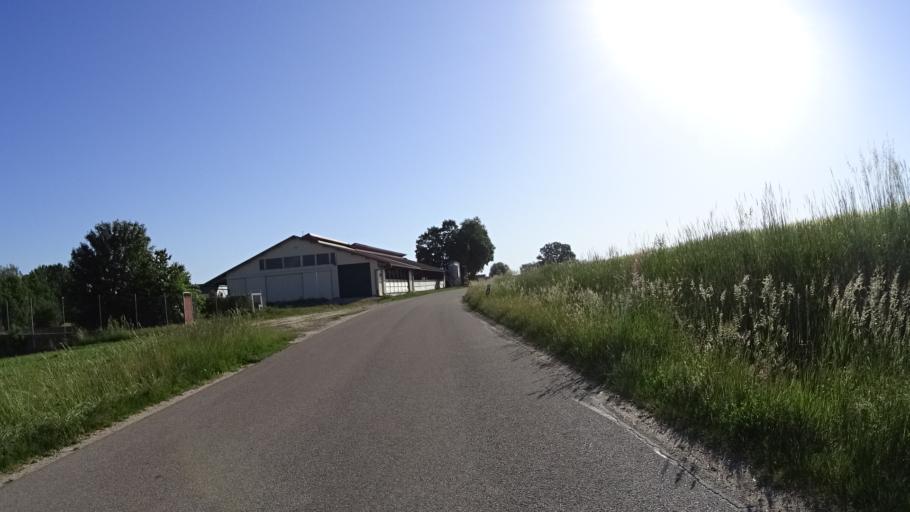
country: DE
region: Bavaria
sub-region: Regierungsbezirk Mittelfranken
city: Burk
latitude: 49.1533
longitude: 10.4610
